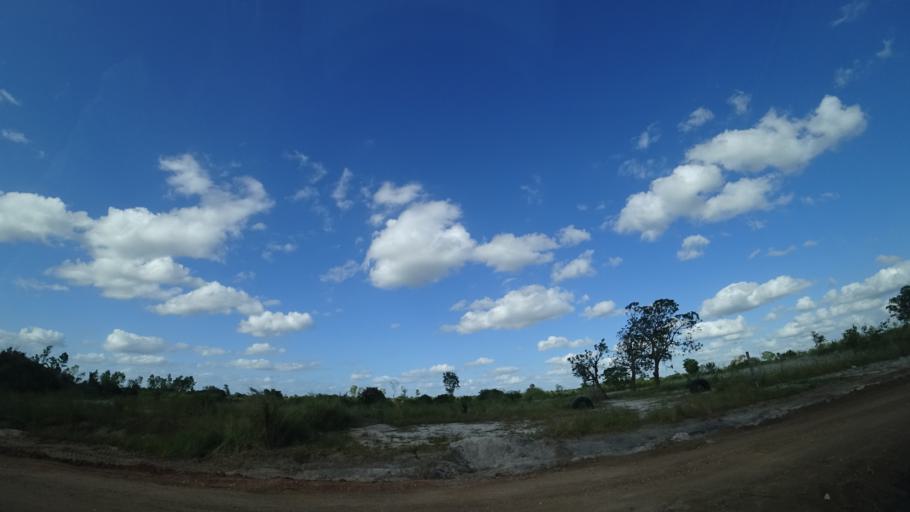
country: MZ
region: Sofala
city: Dondo
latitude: -19.4260
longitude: 34.7076
